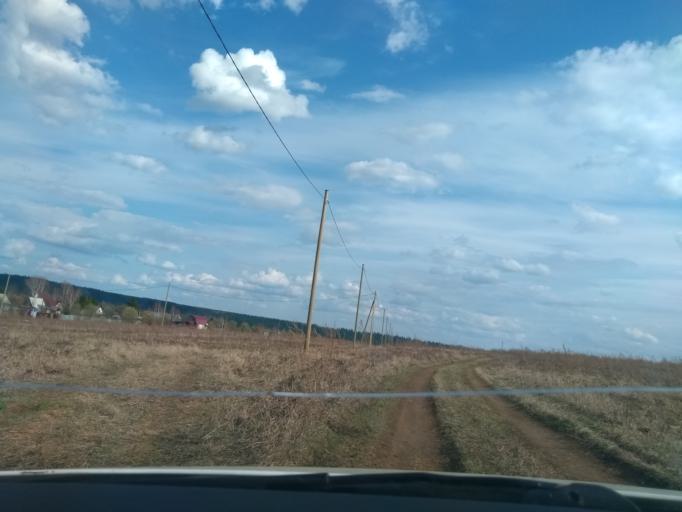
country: RU
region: Perm
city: Sylva
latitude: 57.8436
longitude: 56.7895
